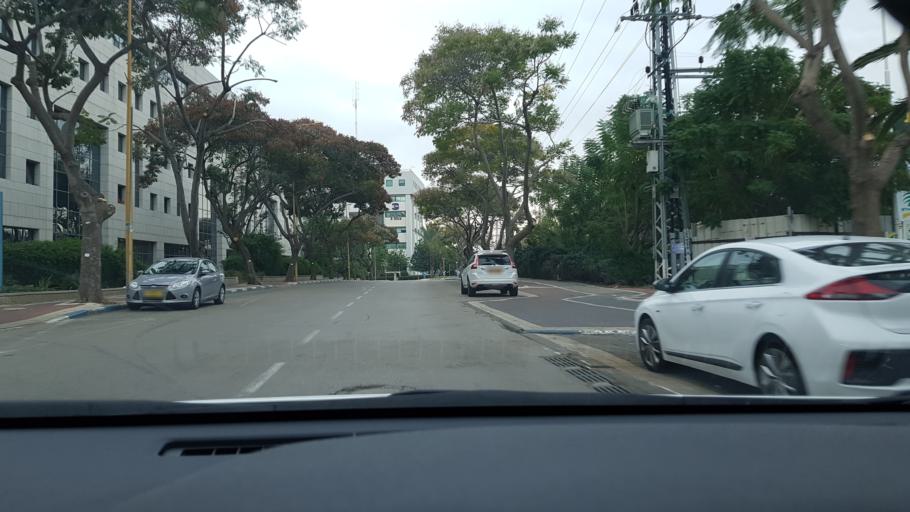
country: IL
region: Central District
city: Ness Ziona
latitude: 31.9108
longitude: 34.8073
